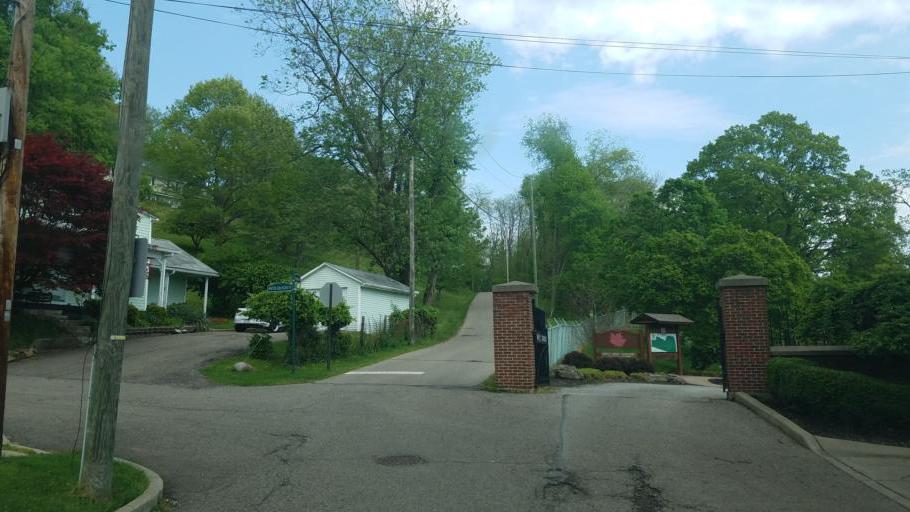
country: US
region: Ohio
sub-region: Licking County
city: Granville
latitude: 40.0654
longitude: -82.5153
